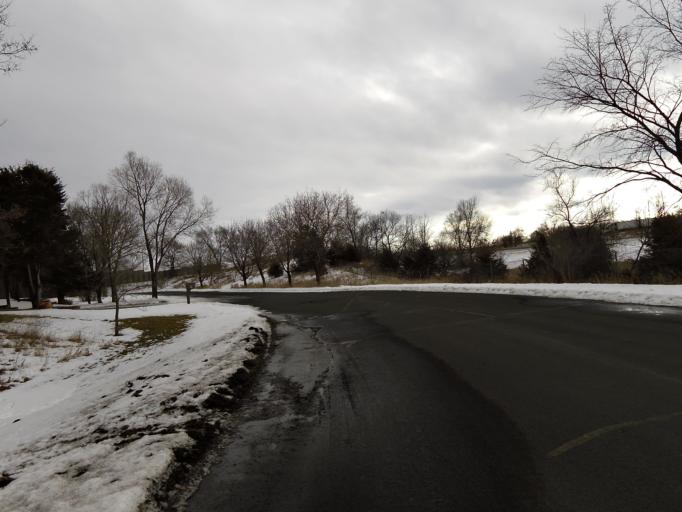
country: US
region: Minnesota
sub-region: Washington County
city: Lakeland
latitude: 44.9638
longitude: -92.7713
